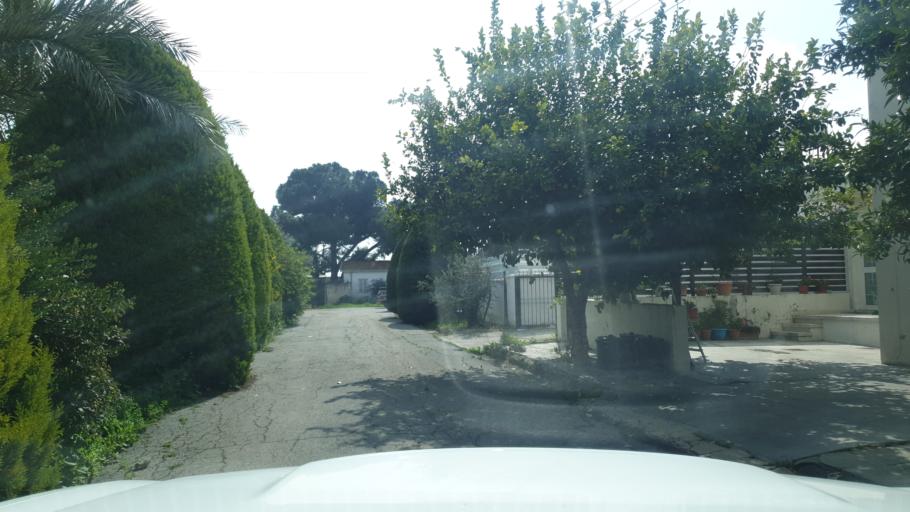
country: CY
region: Lefkosia
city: Kato Deftera
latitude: 35.0857
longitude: 33.2751
